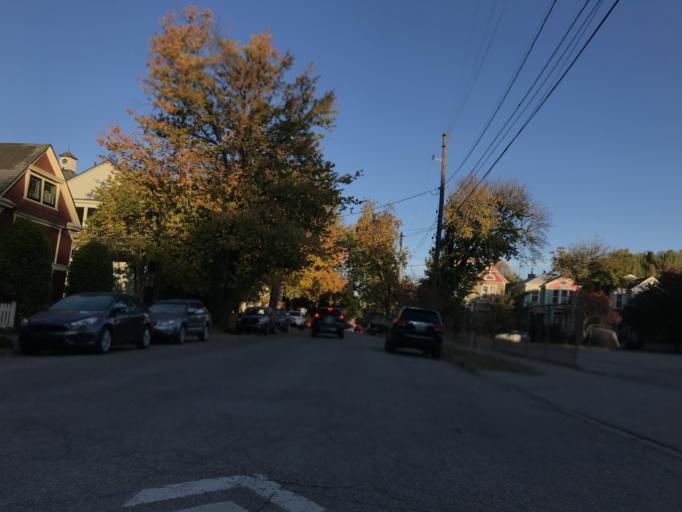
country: US
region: Kentucky
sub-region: Jefferson County
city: Louisville
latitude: 38.2392
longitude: -85.7281
